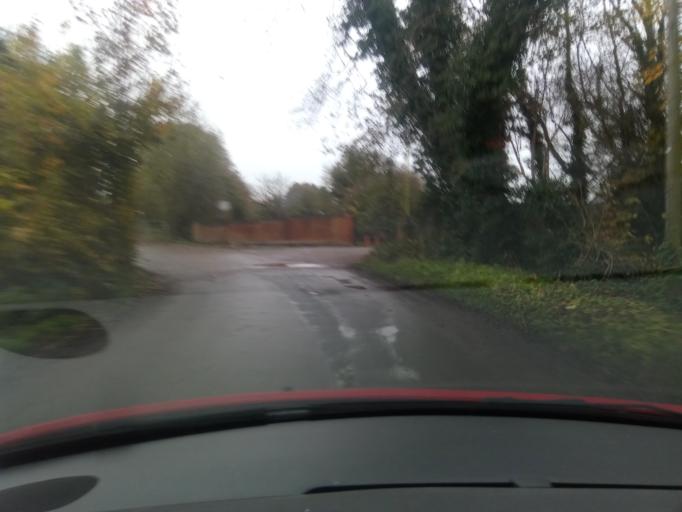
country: GB
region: England
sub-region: Derbyshire
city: Melbourne
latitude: 52.8675
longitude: -1.4243
